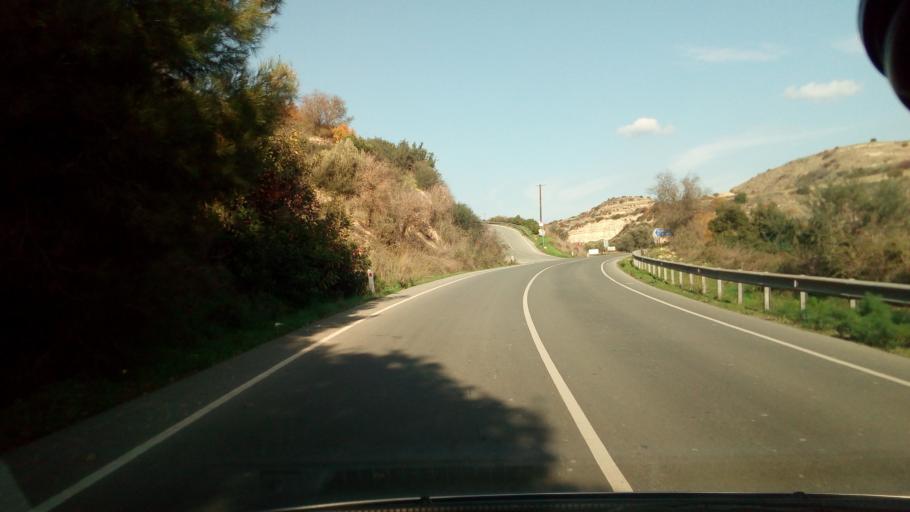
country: CY
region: Pafos
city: Polis
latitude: 34.9632
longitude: 32.4565
